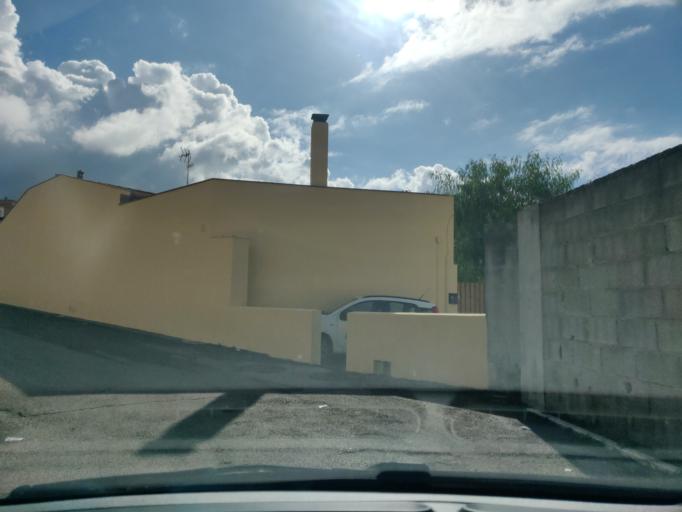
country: IT
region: Latium
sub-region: Citta metropolitana di Roma Capitale
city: Civitavecchia
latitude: 42.0969
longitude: 11.7974
